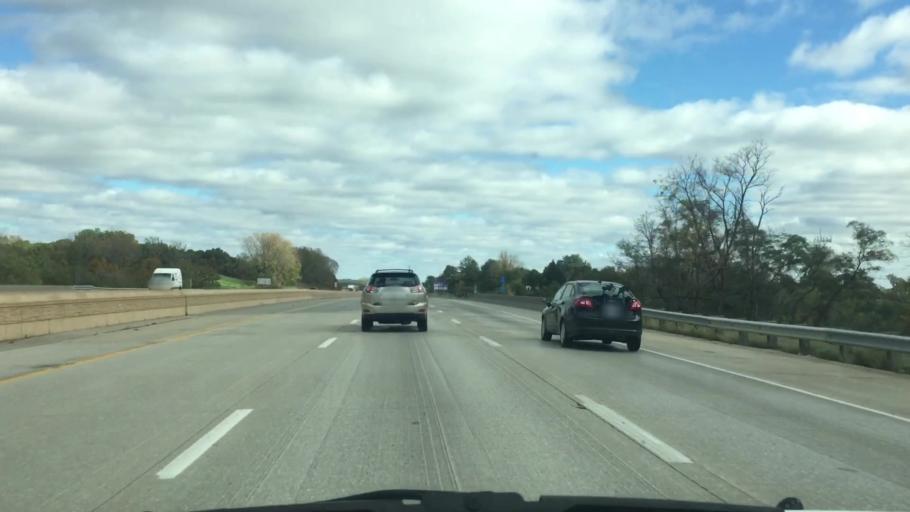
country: US
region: Iowa
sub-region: Johnson County
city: Coralville
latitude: 41.6889
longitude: -91.5813
